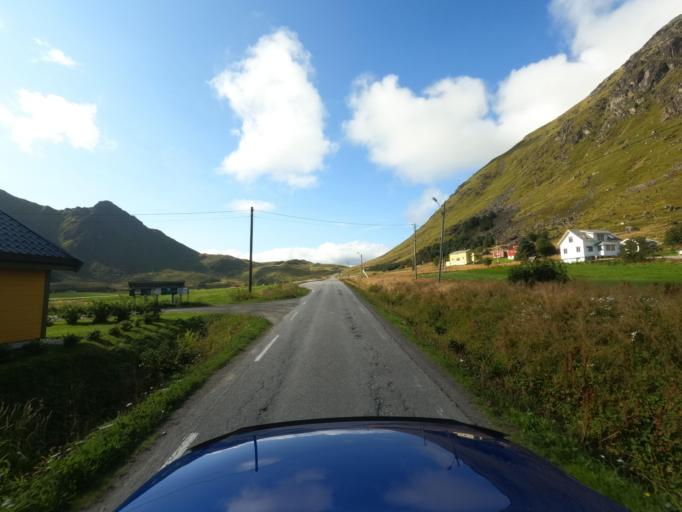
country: NO
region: Nordland
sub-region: Vestvagoy
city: Leknes
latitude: 68.1121
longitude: 13.7016
